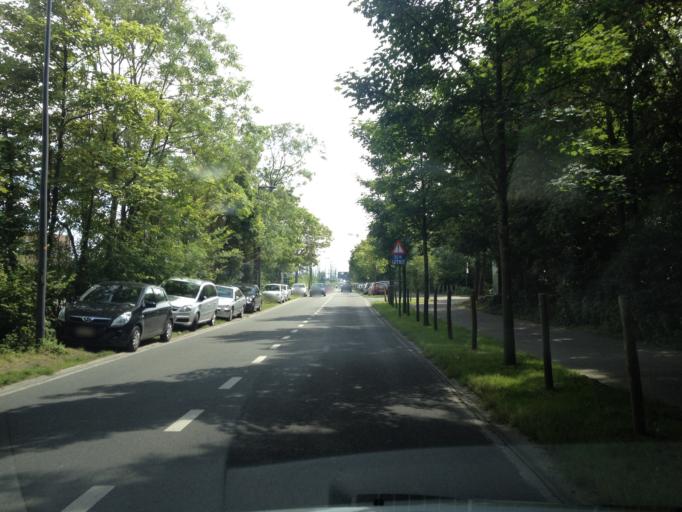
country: BE
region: Flanders
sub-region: Provincie West-Vlaanderen
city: Ostend
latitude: 51.2238
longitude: 2.9289
